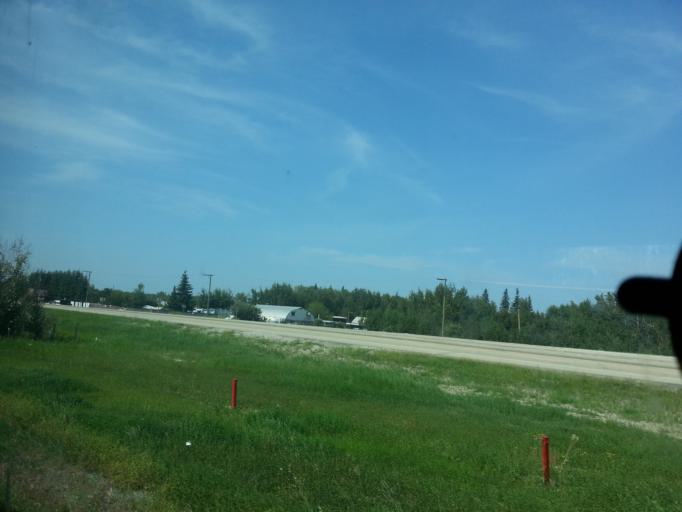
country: CA
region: Alberta
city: Drayton Valley
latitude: 53.5845
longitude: -114.7729
